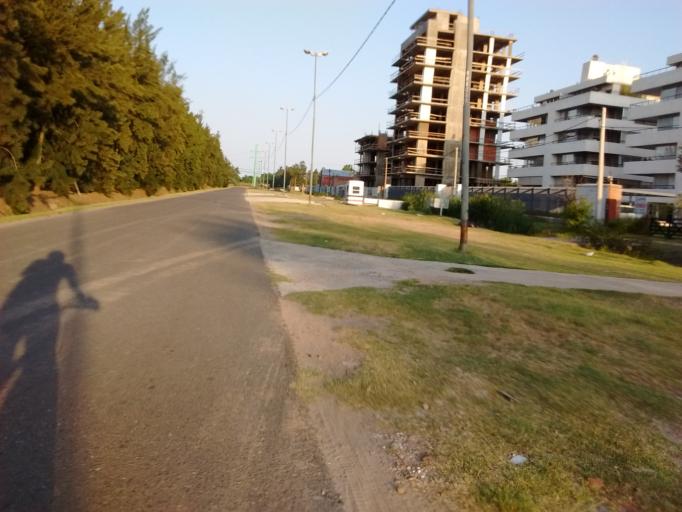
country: AR
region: Santa Fe
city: Funes
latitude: -32.9144
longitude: -60.7553
